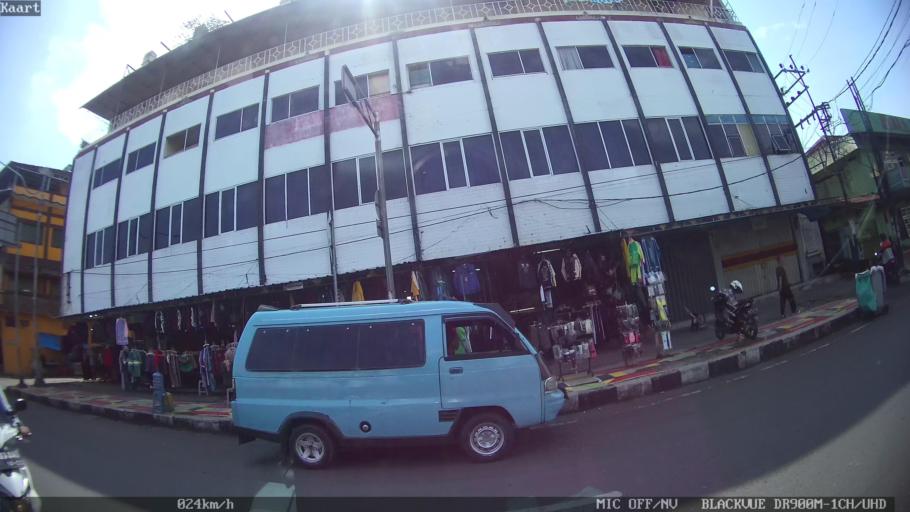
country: ID
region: Lampung
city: Bandarlampung
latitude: -5.4097
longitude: 105.2570
